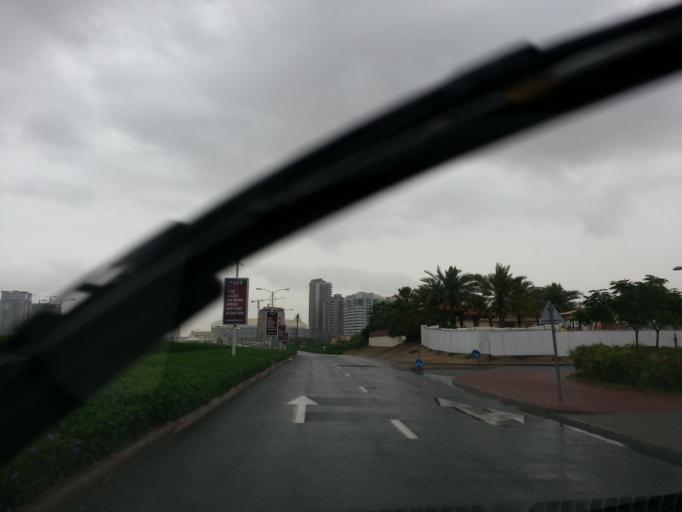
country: AE
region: Dubai
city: Dubai
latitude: 25.0430
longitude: 55.2070
